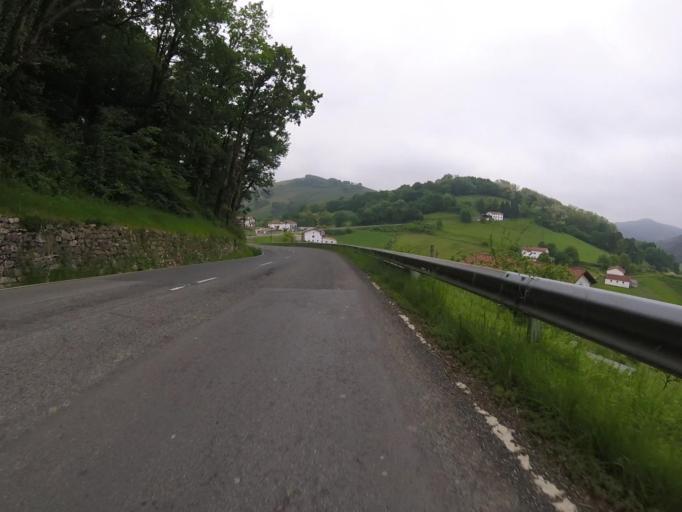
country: ES
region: Navarre
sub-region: Provincia de Navarra
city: Zugarramurdi
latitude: 43.2729
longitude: -1.4953
